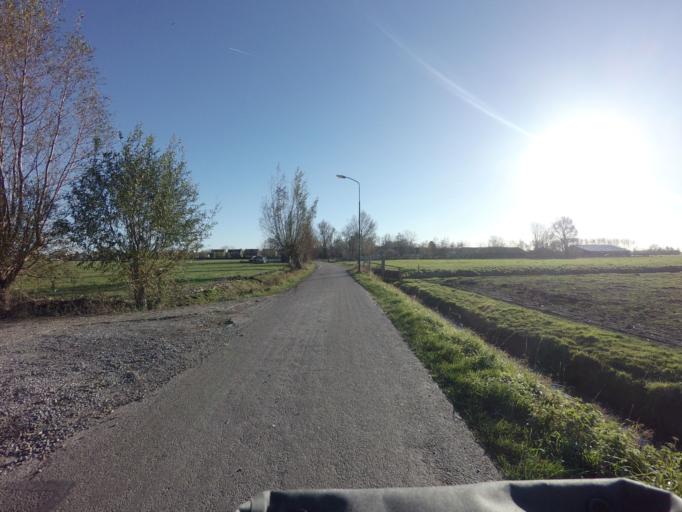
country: NL
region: Utrecht
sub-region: Stichtse Vecht
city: Vreeland
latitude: 52.2504
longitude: 4.9862
